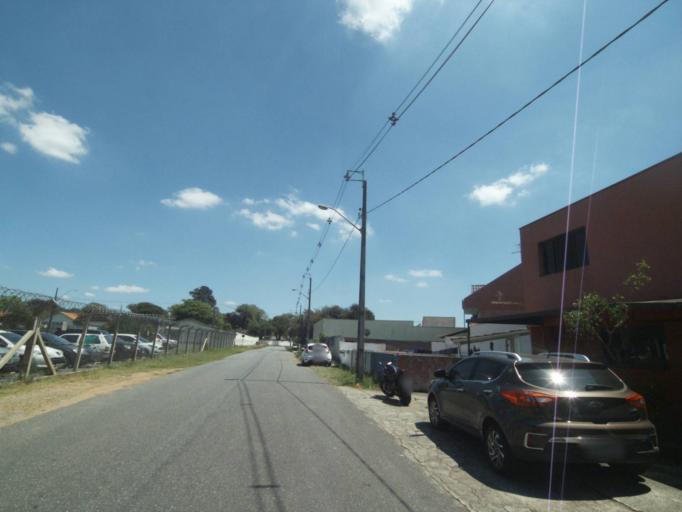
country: BR
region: Parana
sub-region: Curitiba
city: Curitiba
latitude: -25.3990
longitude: -49.2309
